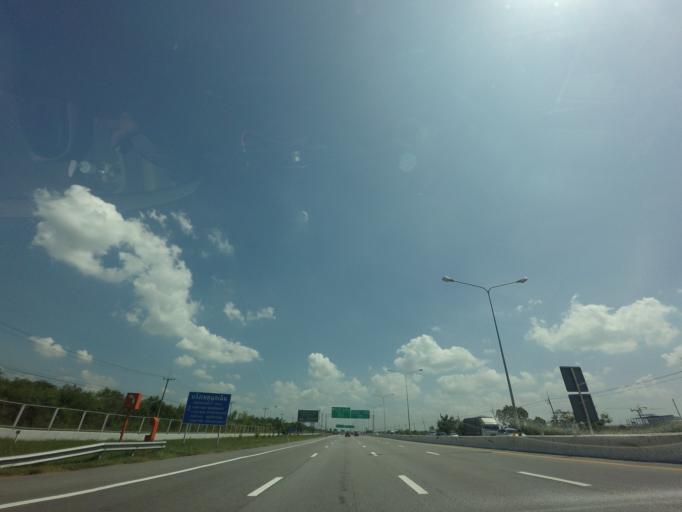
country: TH
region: Chachoengsao
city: Bang Pakong
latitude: 13.6086
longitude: 100.9396
